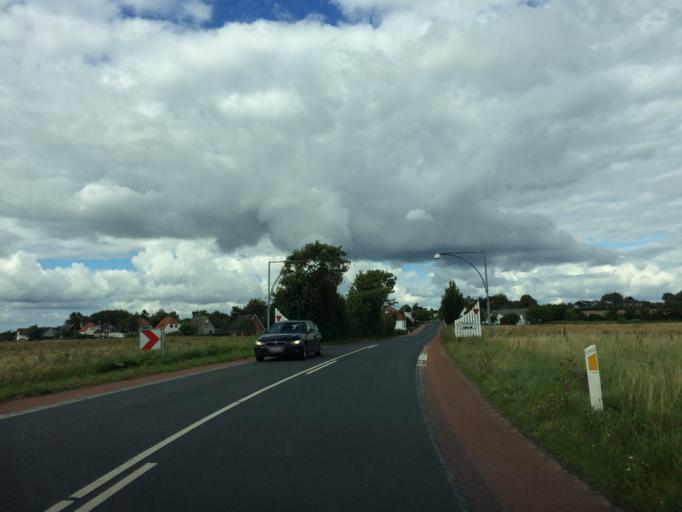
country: DK
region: South Denmark
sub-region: Assens Kommune
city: Harby
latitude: 55.1928
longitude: 10.1525
